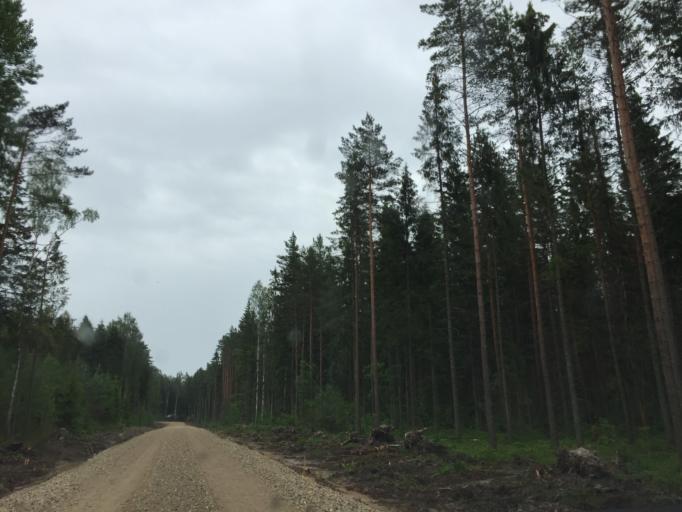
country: LV
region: Tukuma Rajons
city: Tukums
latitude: 57.0048
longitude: 23.1056
